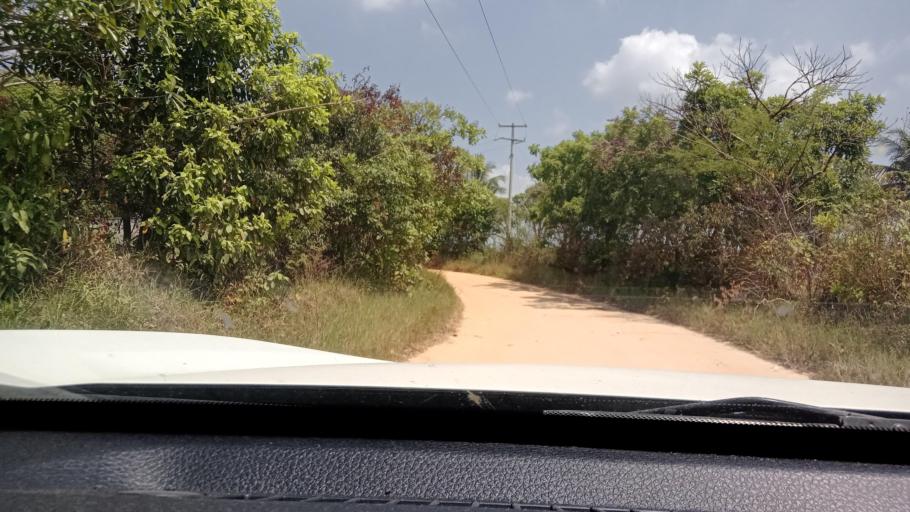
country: MX
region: Veracruz
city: Las Choapas
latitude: 17.9386
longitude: -94.1185
